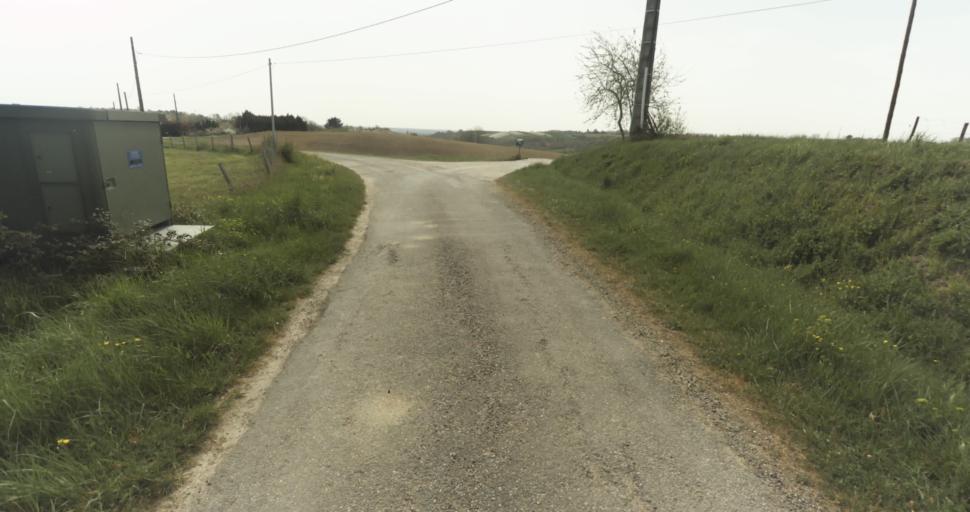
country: FR
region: Midi-Pyrenees
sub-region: Departement du Tarn-et-Garonne
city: Moissac
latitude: 44.1154
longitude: 1.0534
